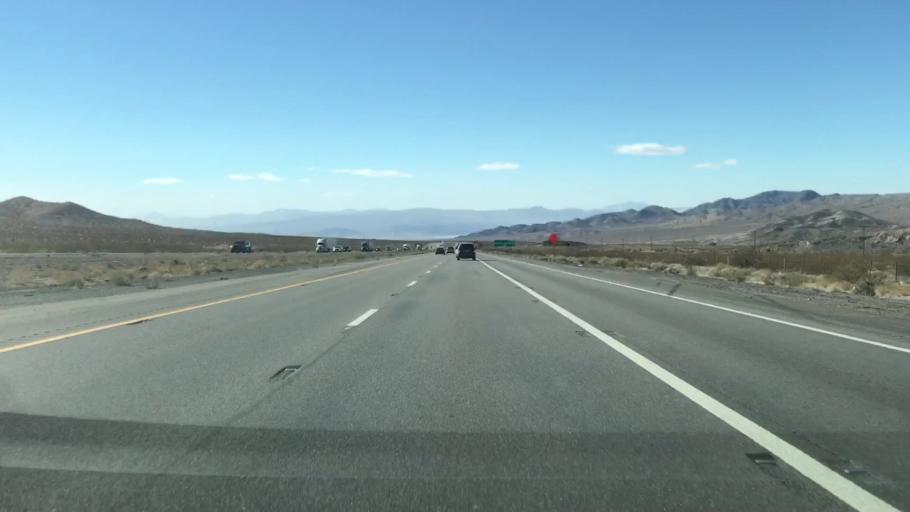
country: US
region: Nevada
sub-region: Clark County
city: Sandy Valley
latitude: 35.3817
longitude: -115.8682
